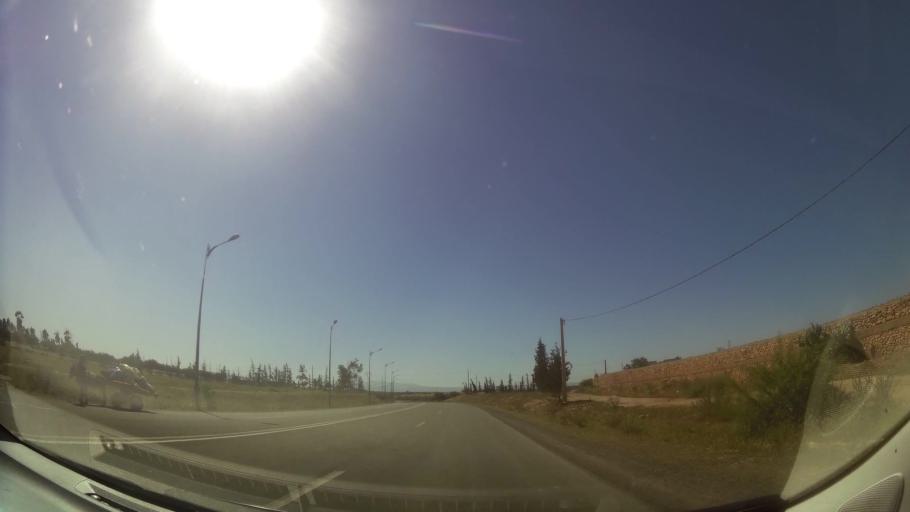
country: MA
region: Oriental
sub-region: Oujda-Angad
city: Oujda
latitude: 34.7384
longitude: -1.8842
